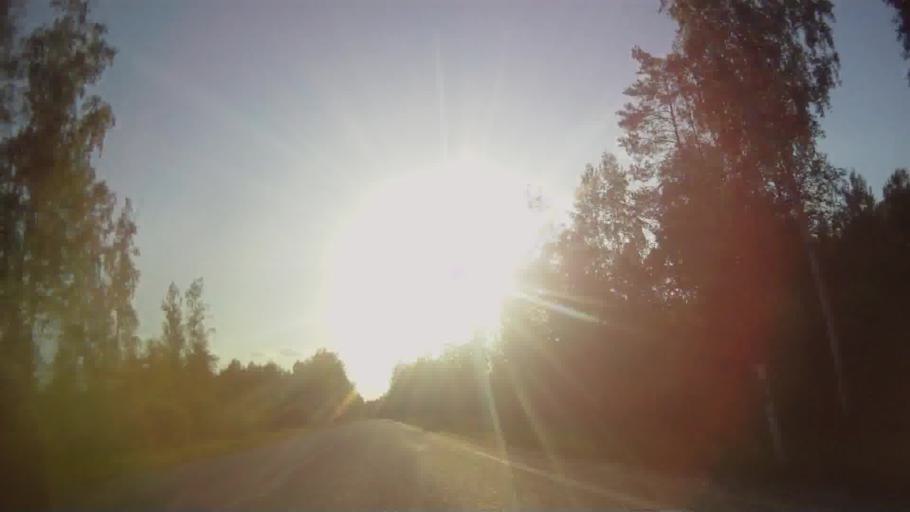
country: LV
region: Livani
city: Livani
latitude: 56.5264
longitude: 26.4056
